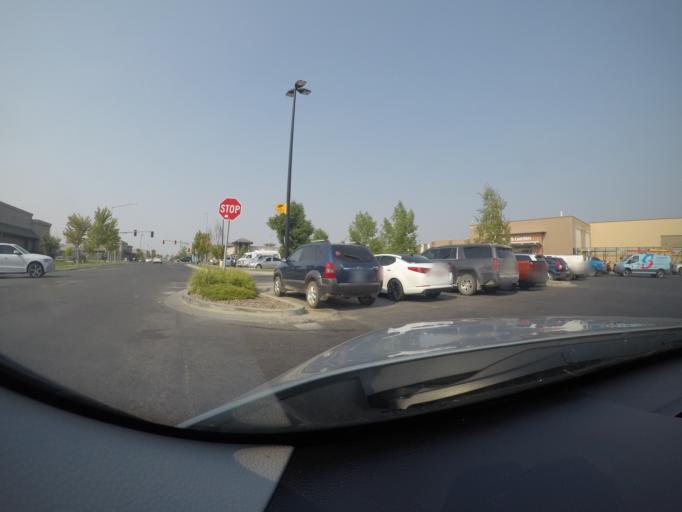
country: US
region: Montana
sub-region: Flathead County
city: Kalispell
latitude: 48.2322
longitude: -114.3277
